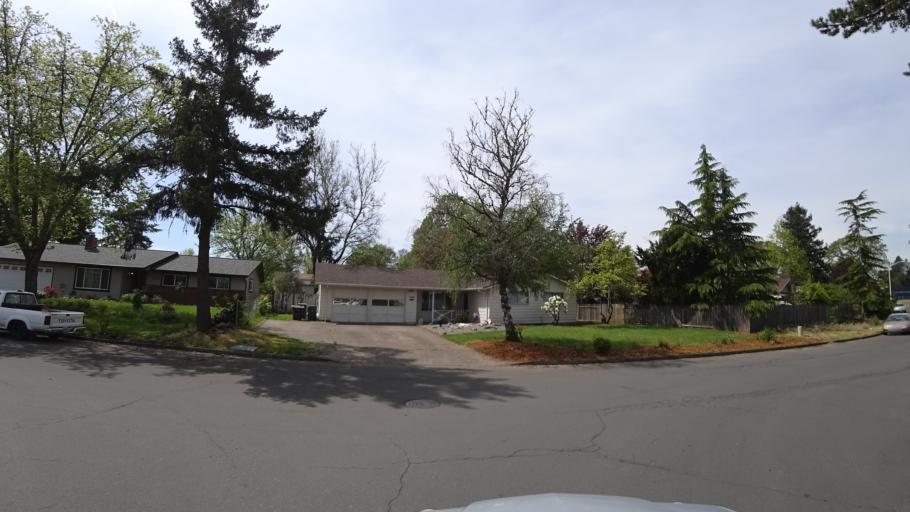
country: US
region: Oregon
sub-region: Washington County
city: Hillsboro
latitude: 45.5290
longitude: -122.9625
